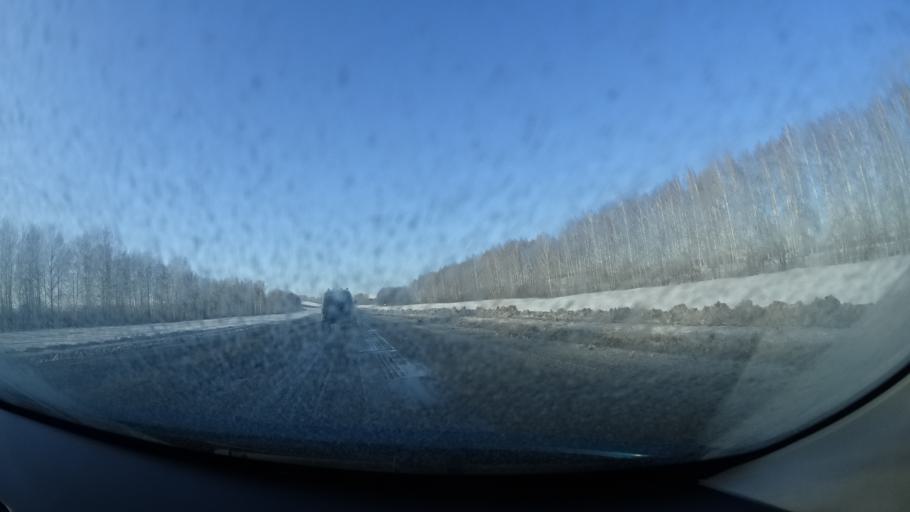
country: RU
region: Bashkortostan
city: Birsk
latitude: 55.2721
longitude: 55.7246
